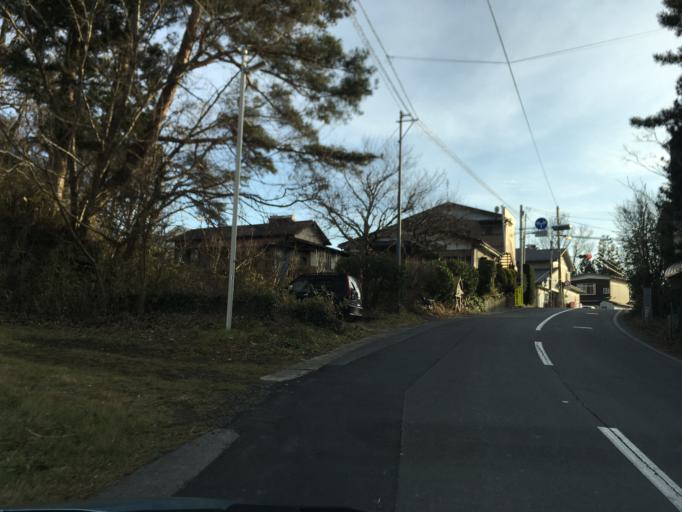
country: JP
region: Iwate
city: Ichinoseki
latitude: 38.7820
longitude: 141.2235
